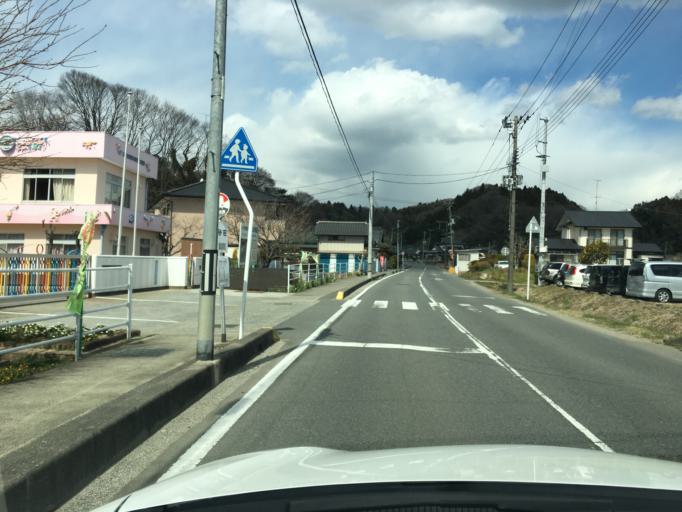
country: JP
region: Fukushima
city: Iwaki
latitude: 37.0606
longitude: 140.9107
